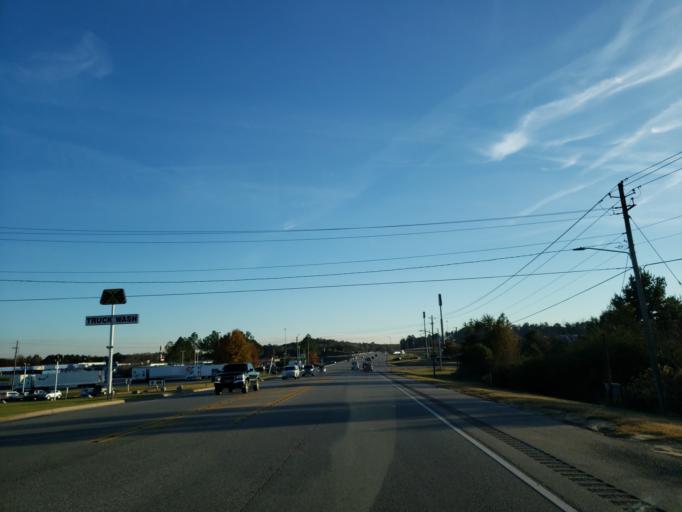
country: US
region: Alabama
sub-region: Tuscaloosa County
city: Holt
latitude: 33.1786
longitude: -87.4475
